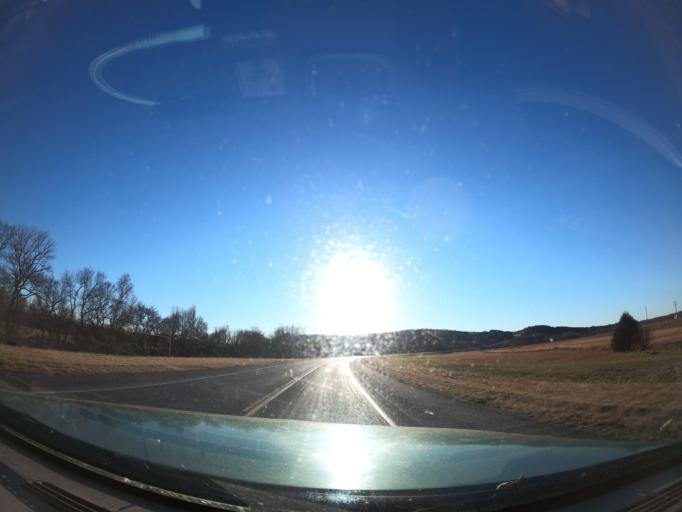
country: US
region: Oklahoma
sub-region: Pittsburg County
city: Hartshorne
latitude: 34.8926
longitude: -95.4402
